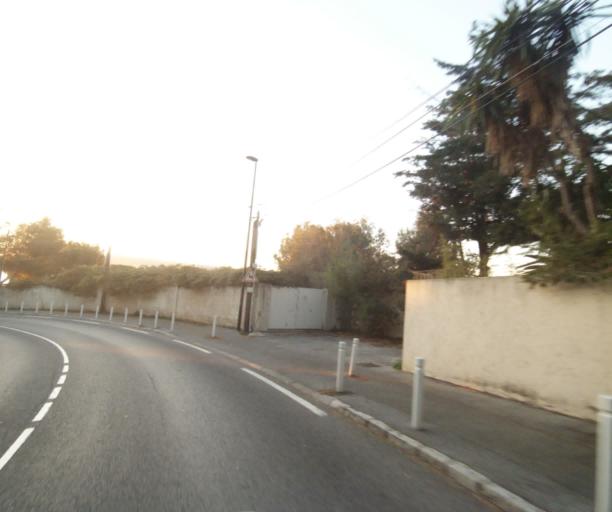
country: FR
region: Provence-Alpes-Cote d'Azur
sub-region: Departement des Alpes-Maritimes
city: Antibes
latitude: 43.5496
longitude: 7.1194
